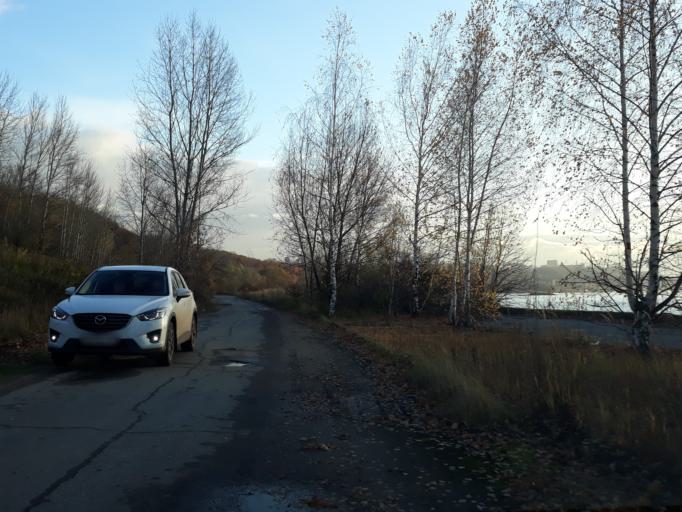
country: RU
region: Nizjnij Novgorod
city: Nizhniy Novgorod
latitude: 56.2741
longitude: 43.9698
